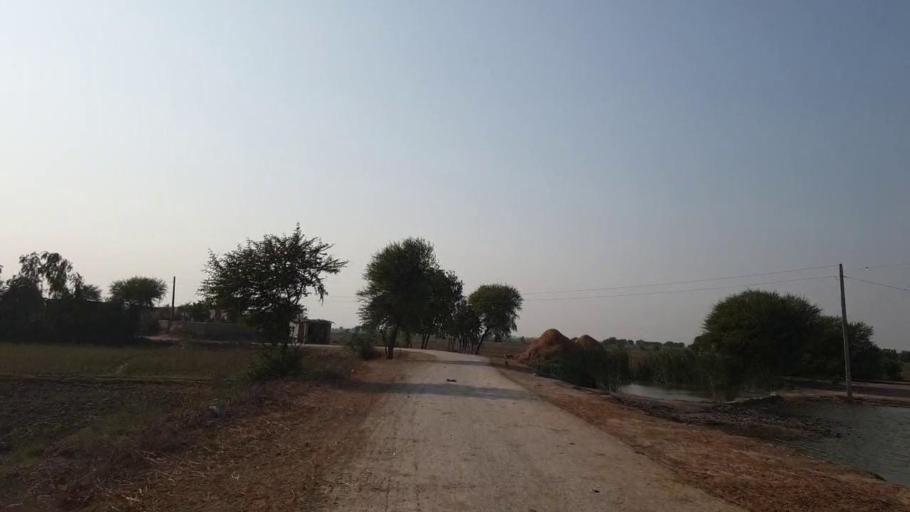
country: PK
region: Sindh
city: Bulri
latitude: 25.0035
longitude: 68.3768
